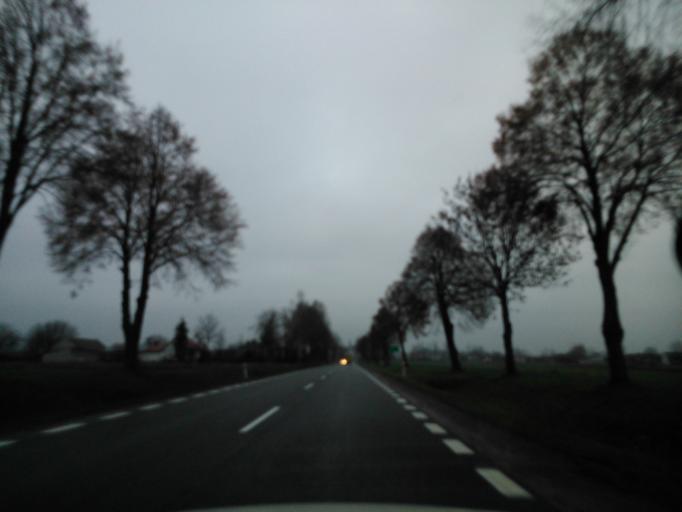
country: PL
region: Swietokrzyskie
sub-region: Powiat opatowski
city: Wojciechowice
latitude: 50.8398
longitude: 21.6375
